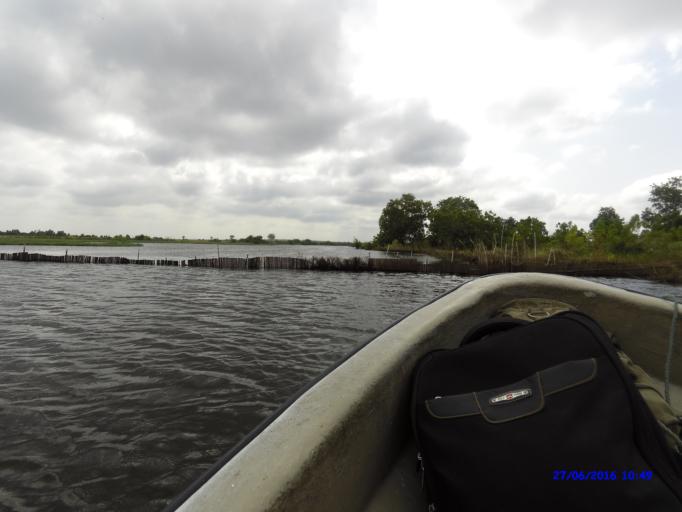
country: BJ
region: Mono
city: Come
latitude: 6.3674
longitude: 1.9263
